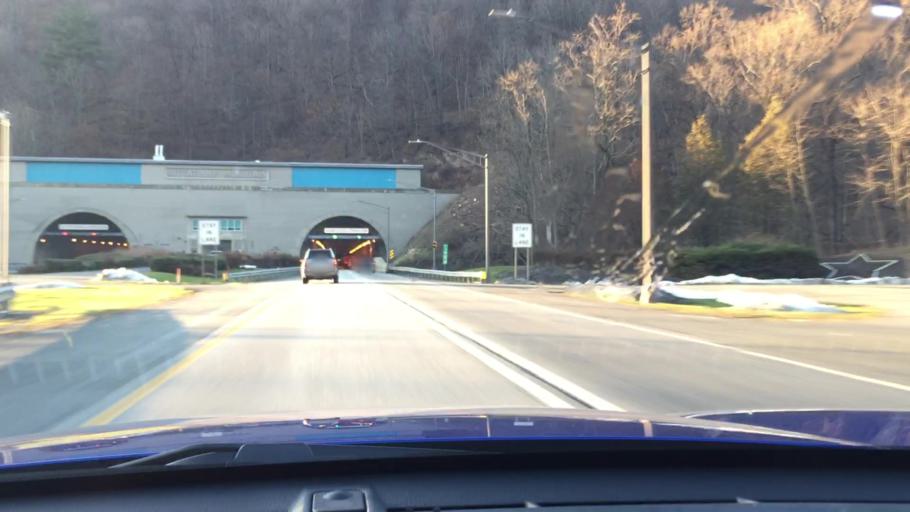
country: US
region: Pennsylvania
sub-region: Franklin County
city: Doylestown
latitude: 40.1493
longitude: -77.6607
